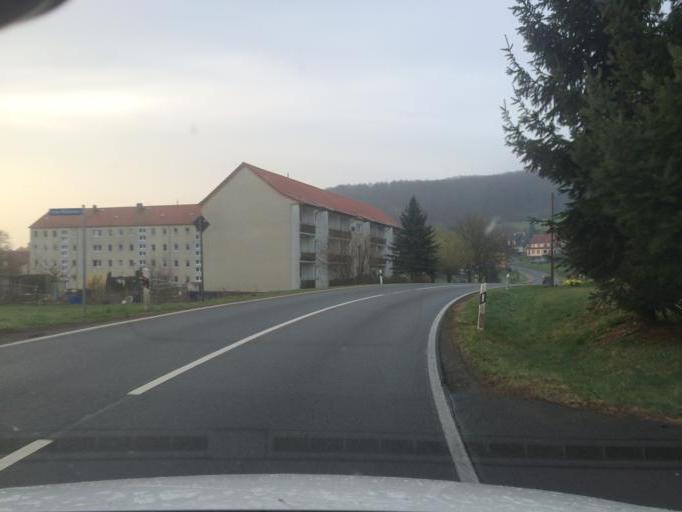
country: DE
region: Thuringia
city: Weissenborn-Luderode
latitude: 51.5358
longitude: 10.4095
